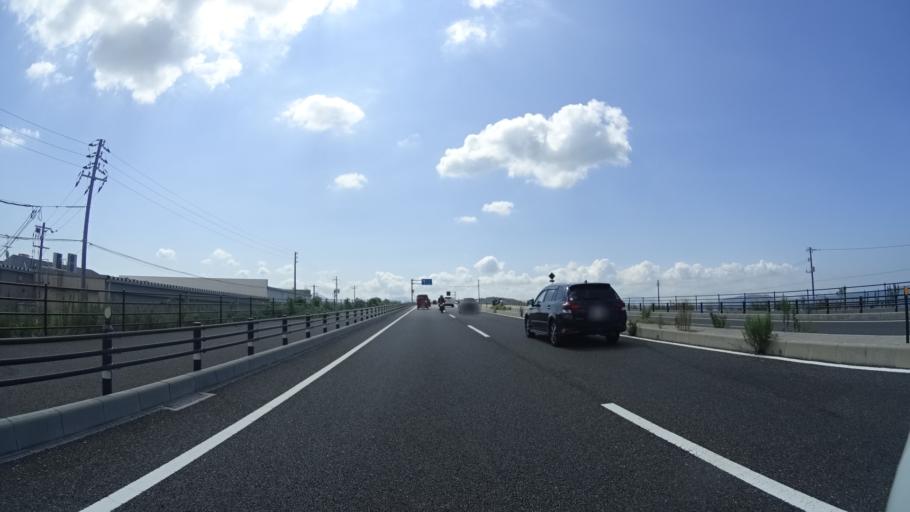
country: JP
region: Yamaguchi
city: Shimonoseki
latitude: 34.0191
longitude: 130.9174
